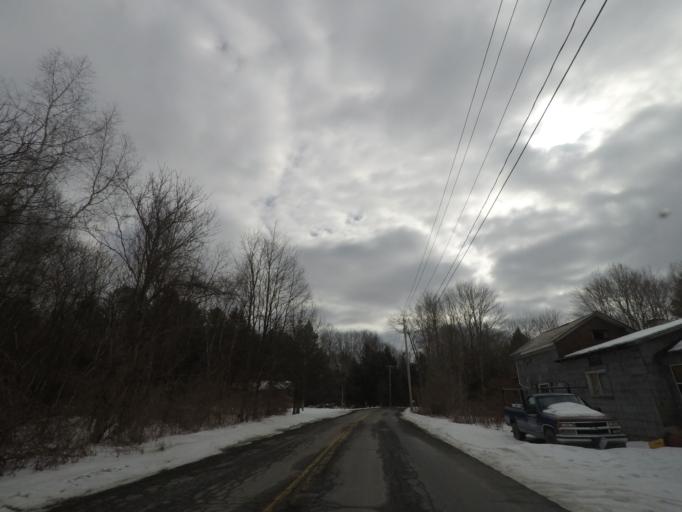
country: US
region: New York
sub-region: Rensselaer County
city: Hoosick Falls
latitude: 42.9433
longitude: -73.4327
